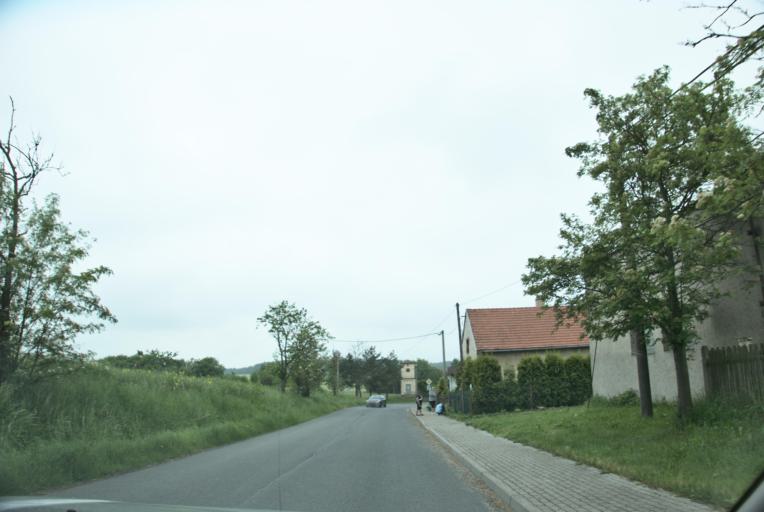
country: CZ
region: Plzensky
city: Zihle
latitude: 50.0137
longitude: 13.4053
